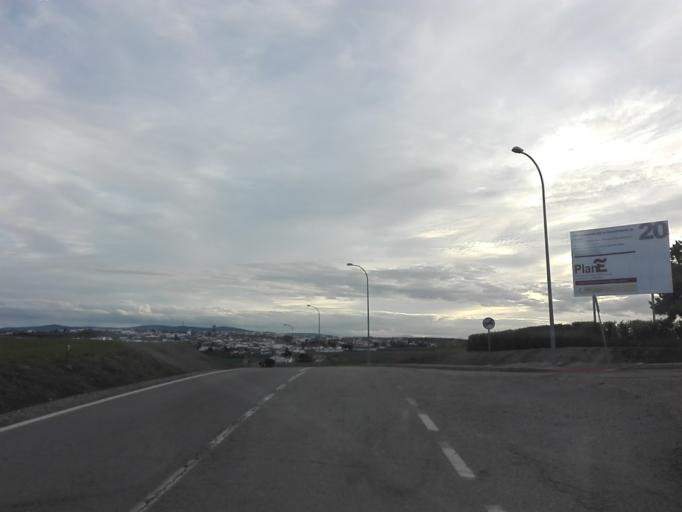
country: ES
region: Extremadura
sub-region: Provincia de Badajoz
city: Usagre
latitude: 38.3678
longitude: -6.1634
